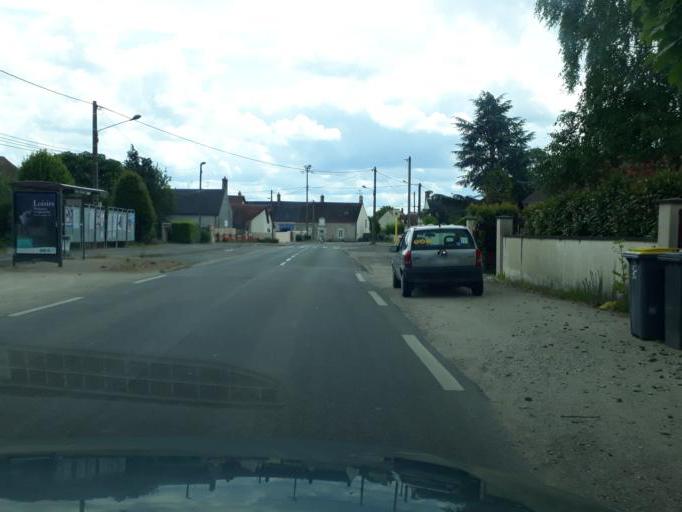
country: FR
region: Centre
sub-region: Departement du Loiret
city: Ingre
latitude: 47.9076
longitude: 1.8340
